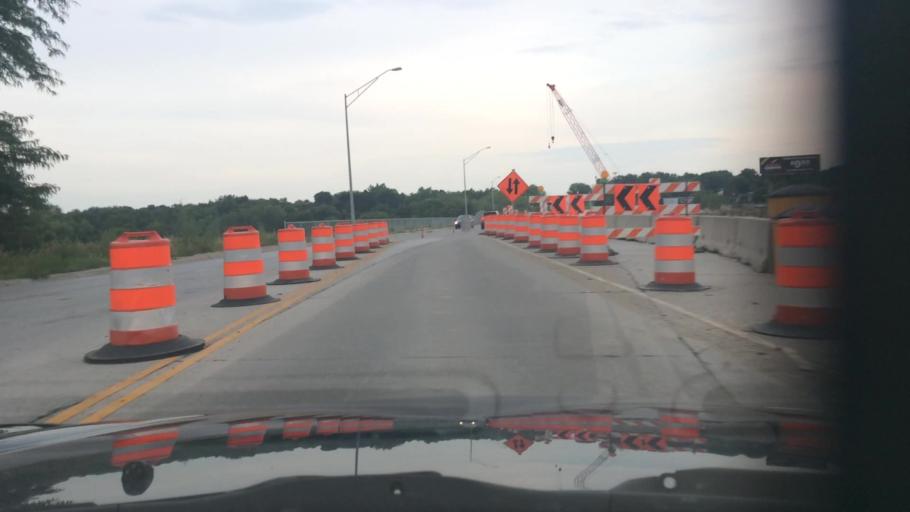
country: US
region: Nebraska
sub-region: Douglas County
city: Ralston
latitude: 41.2003
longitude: -96.0431
